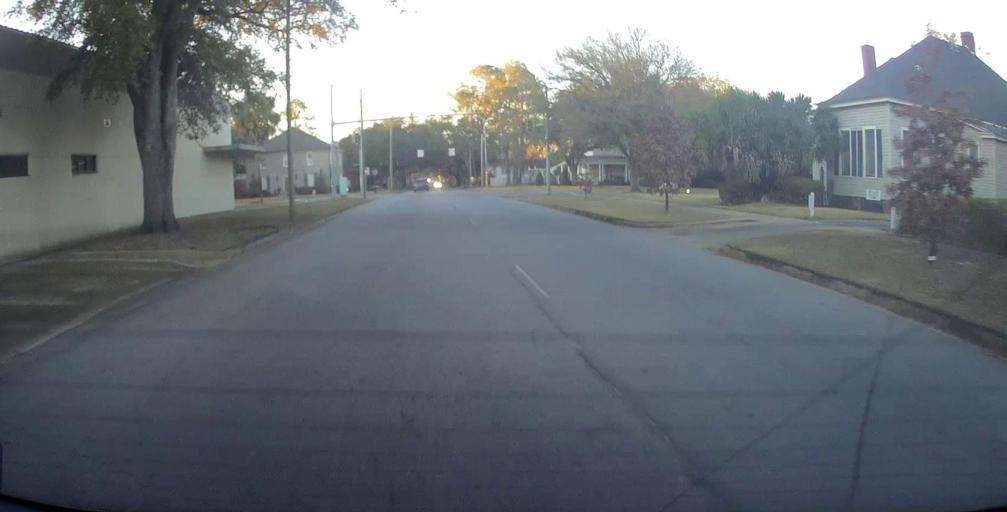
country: US
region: Georgia
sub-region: Dougherty County
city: Albany
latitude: 31.5779
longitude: -84.1619
